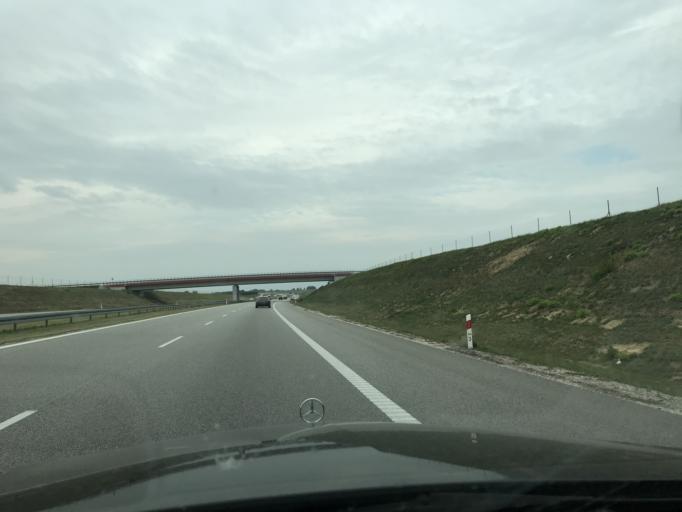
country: PL
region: Subcarpathian Voivodeship
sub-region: Powiat debicki
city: Czarna
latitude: 50.0904
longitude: 21.3021
